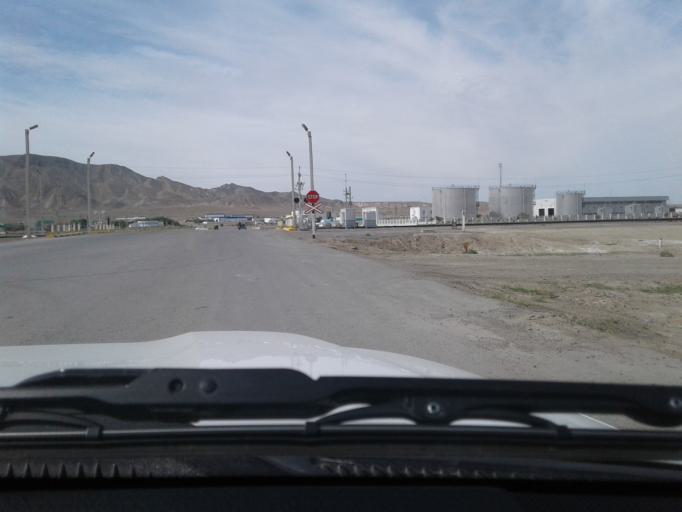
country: TM
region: Balkan
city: Gazanjyk
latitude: 39.2556
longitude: 55.4917
